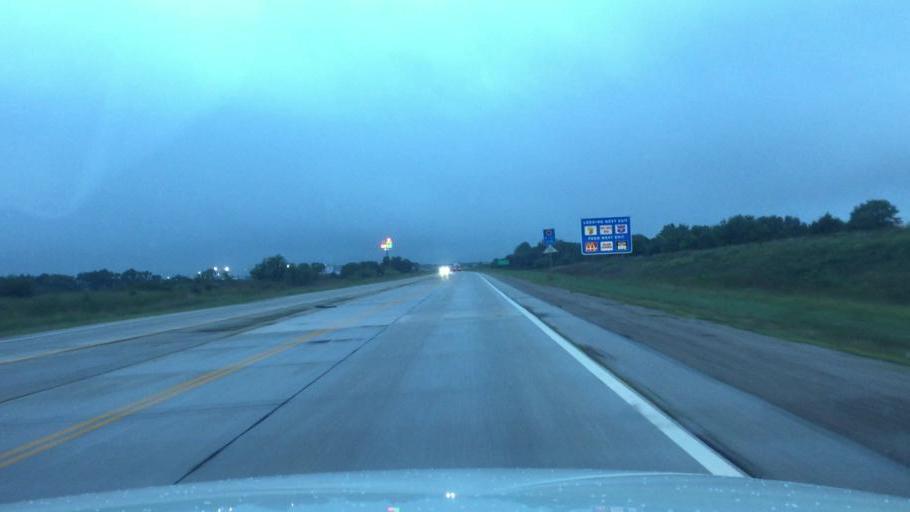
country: US
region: Kansas
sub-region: Neosho County
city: Chanute
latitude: 37.6578
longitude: -95.4796
